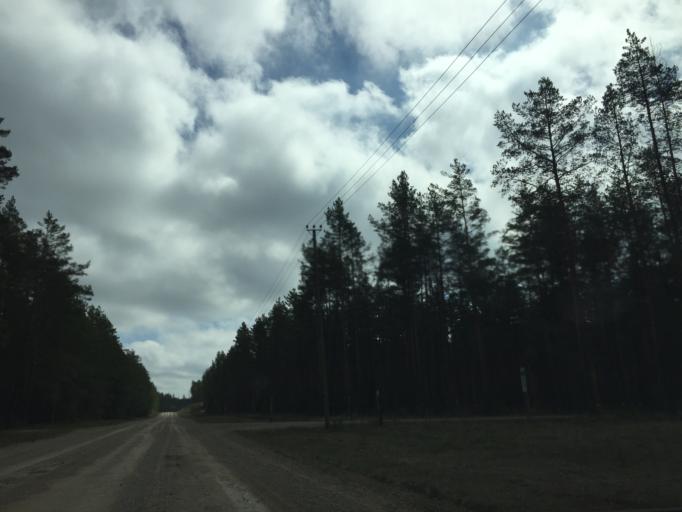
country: EE
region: Valgamaa
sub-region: Valga linn
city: Valga
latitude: 57.6545
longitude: 26.2126
